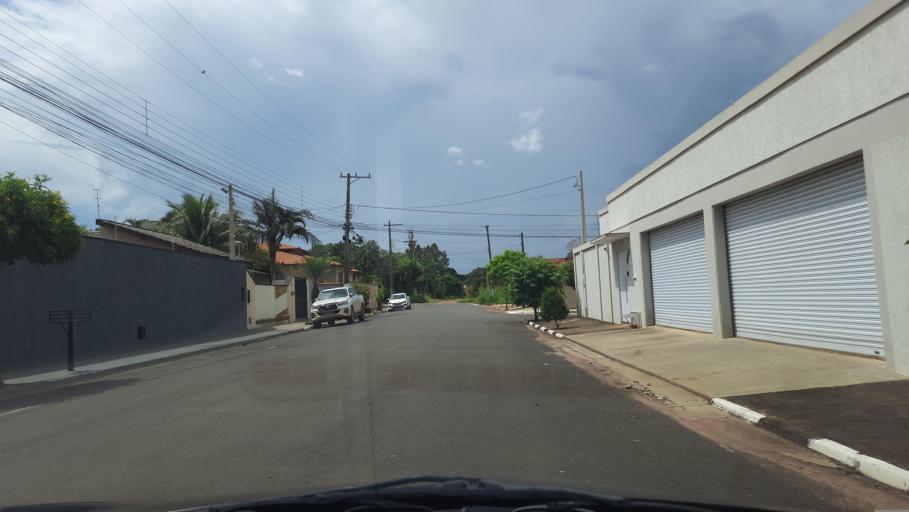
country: BR
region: Sao Paulo
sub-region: Casa Branca
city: Casa Branca
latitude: -21.7803
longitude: -47.0640
